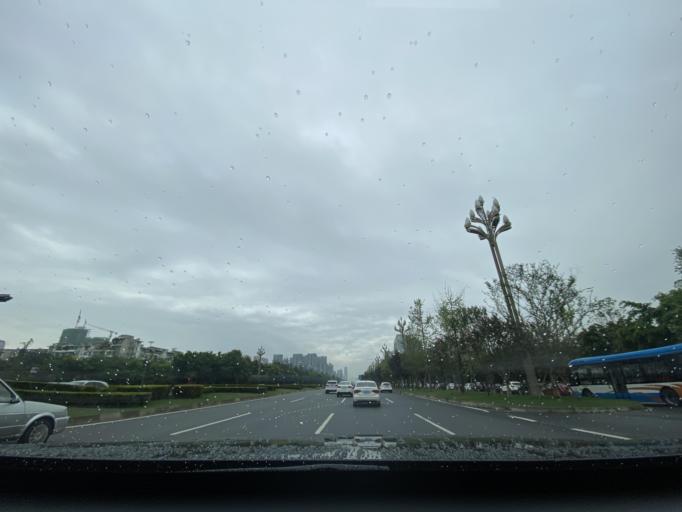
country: CN
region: Sichuan
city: Chengdu
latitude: 30.5262
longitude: 104.0672
